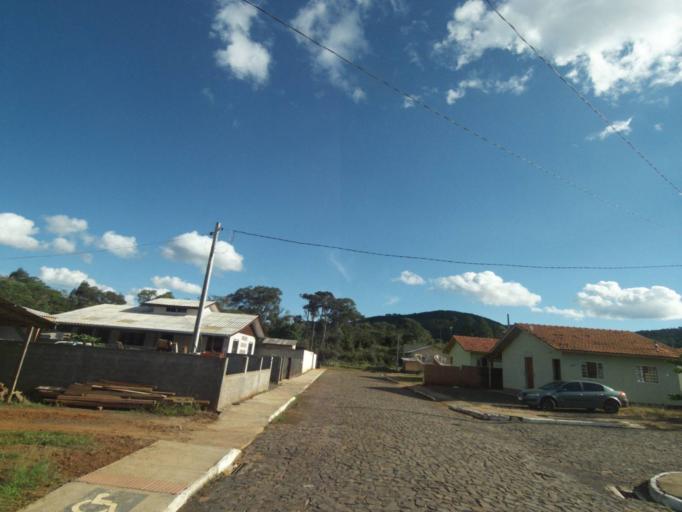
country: BR
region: Parana
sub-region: Uniao Da Vitoria
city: Uniao da Vitoria
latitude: -26.1616
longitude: -51.5321
